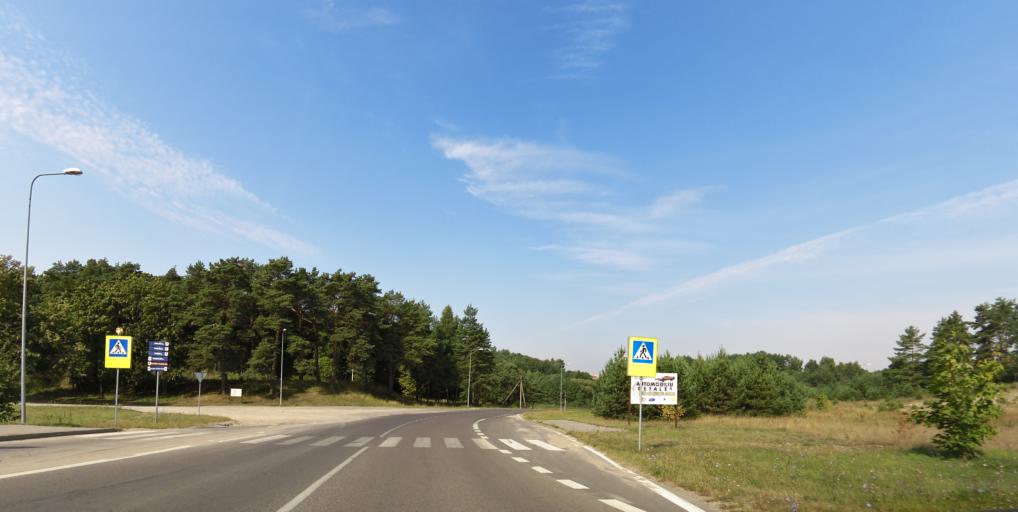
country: LT
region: Vilnius County
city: Pilaite
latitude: 54.7042
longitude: 25.1969
